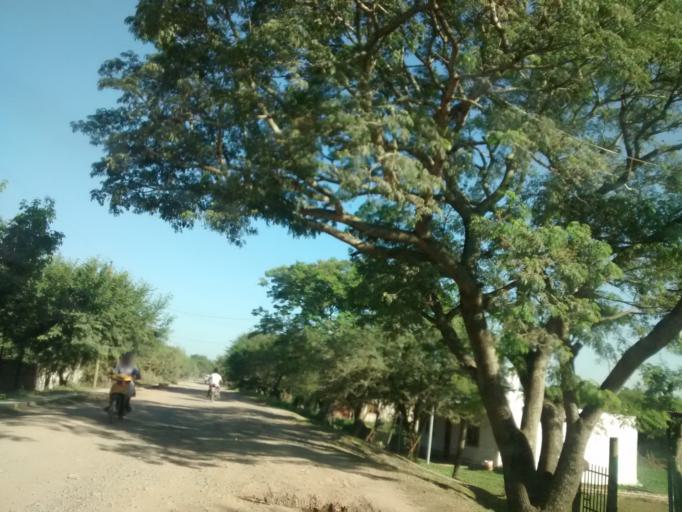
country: AR
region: Chaco
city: Resistencia
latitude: -27.4583
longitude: -58.9613
